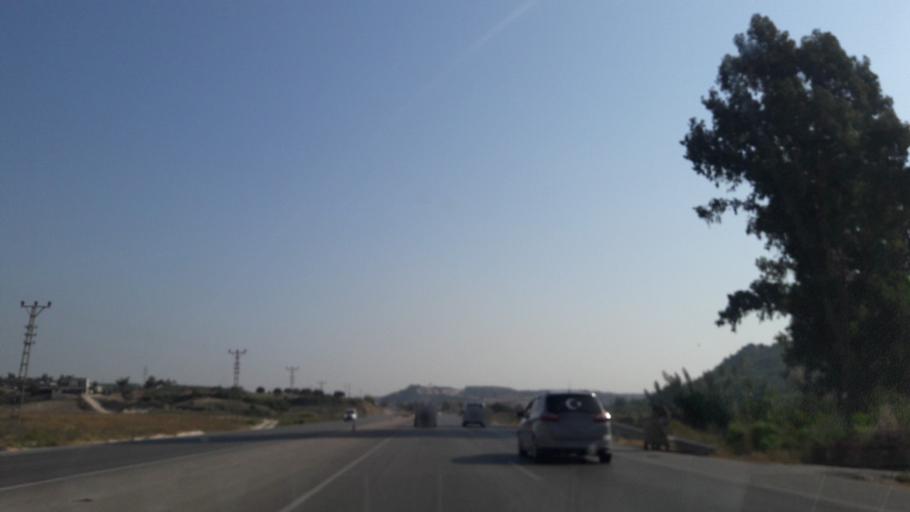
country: TR
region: Adana
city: Yuregir
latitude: 37.0683
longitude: 35.4532
